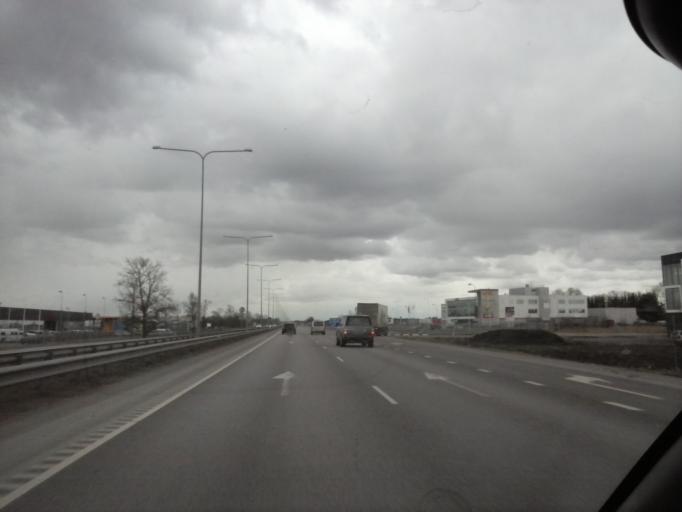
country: EE
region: Harju
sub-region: Tallinna linn
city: Tallinn
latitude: 59.3998
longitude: 24.8162
